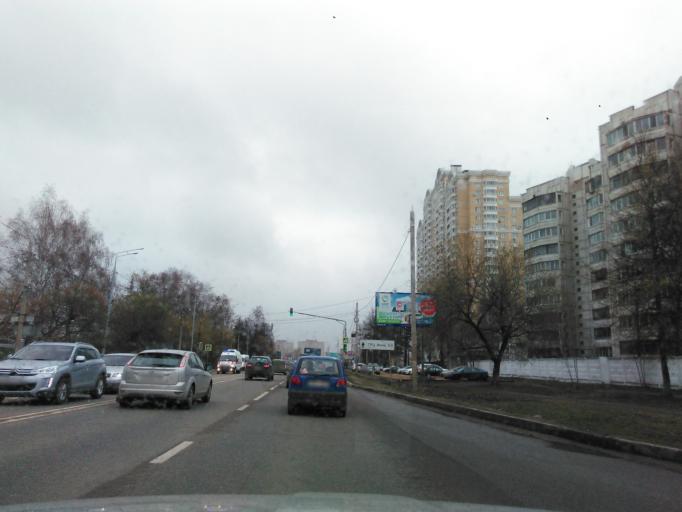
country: RU
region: Moskovskaya
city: Opalikha
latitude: 55.8338
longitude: 37.2808
